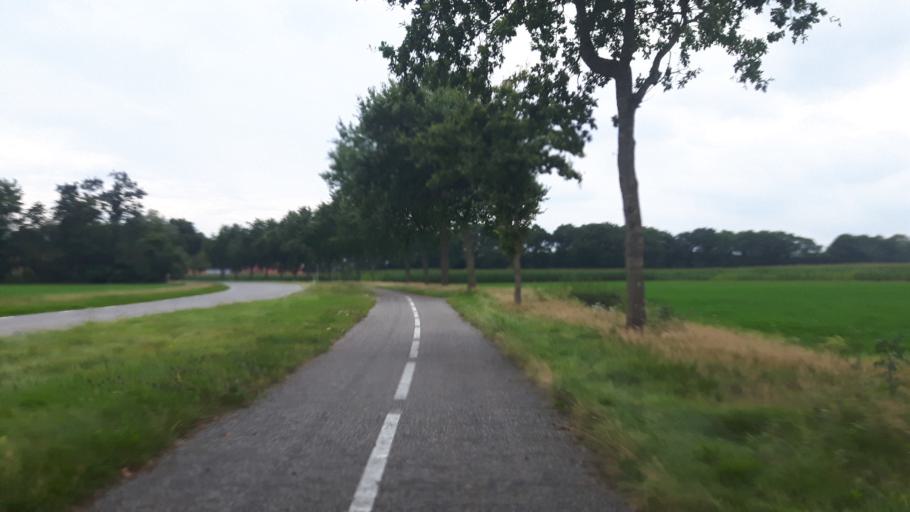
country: NL
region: Friesland
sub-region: Gemeente Weststellingwerf
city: Noordwolde
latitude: 52.9604
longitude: 6.2200
